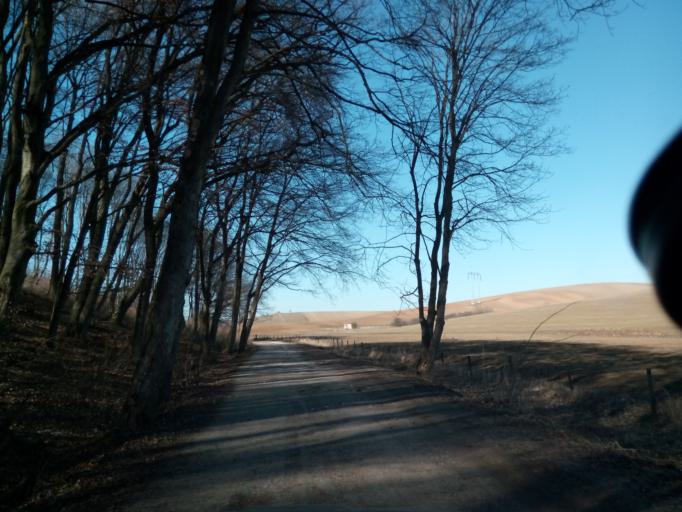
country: SK
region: Kosicky
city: Roznava
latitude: 48.5487
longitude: 20.5414
